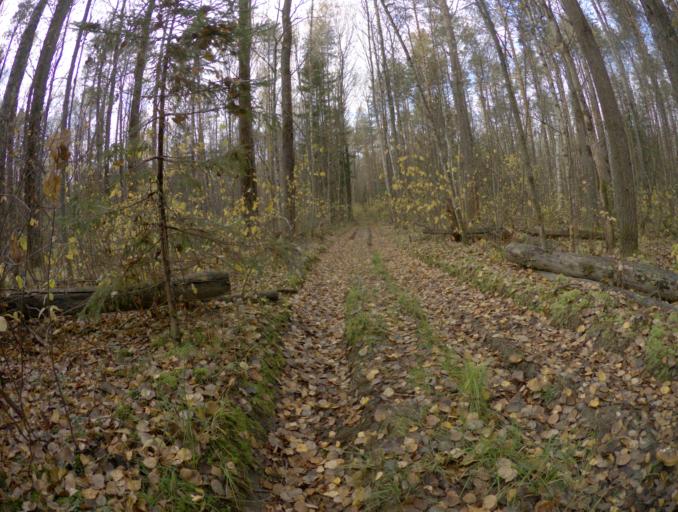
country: RU
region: Vladimir
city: Raduzhnyy
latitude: 55.9645
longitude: 40.3680
